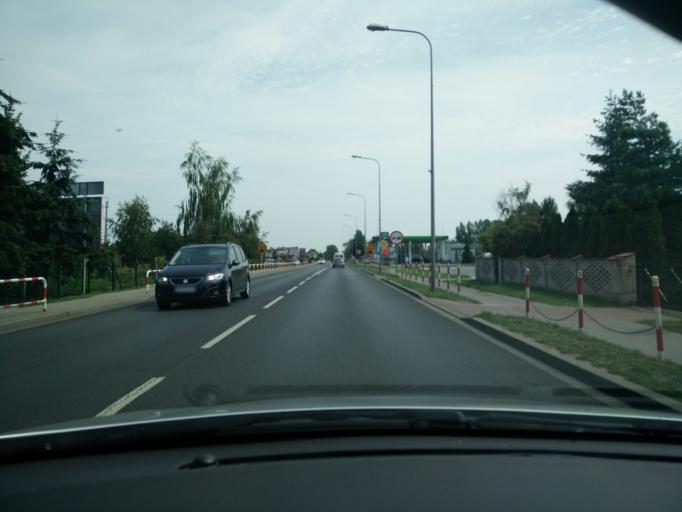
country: PL
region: Greater Poland Voivodeship
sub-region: Powiat slupecki
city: Strzalkowo
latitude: 52.3079
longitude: 17.8238
